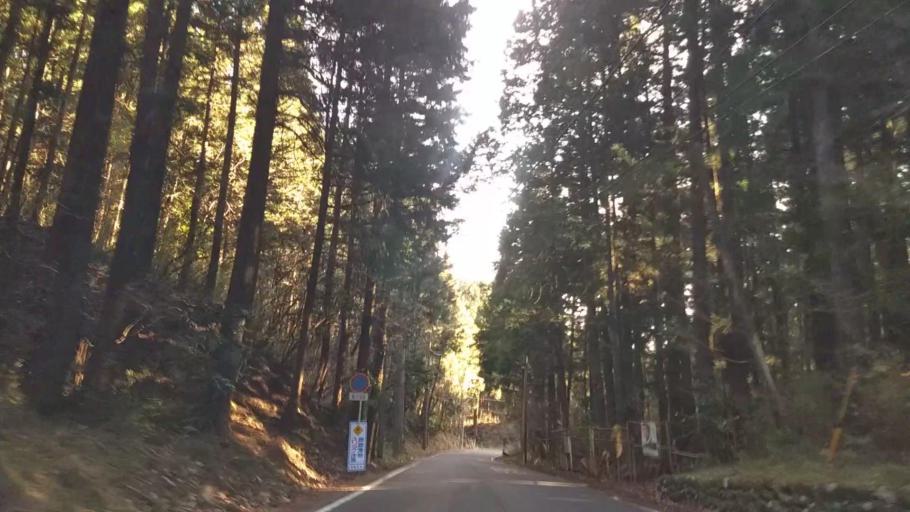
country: JP
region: Yamanashi
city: Uenohara
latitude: 35.5548
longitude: 139.2113
